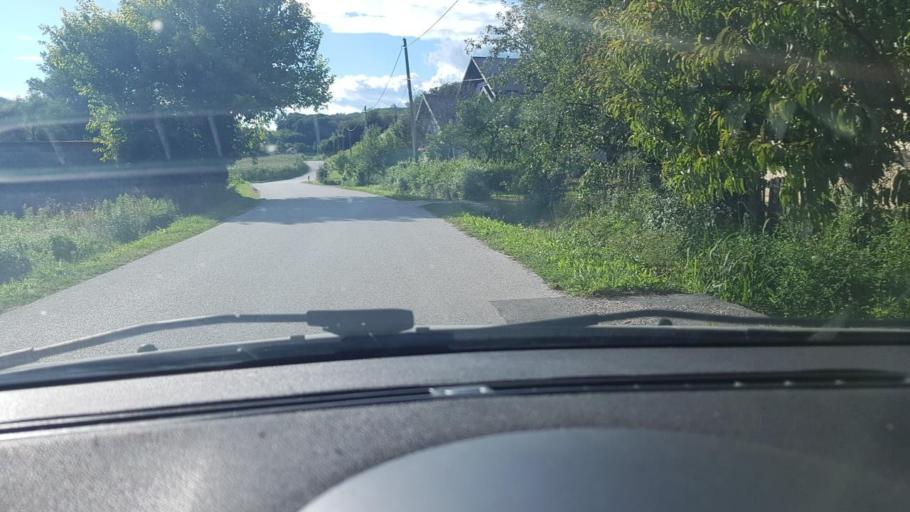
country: HR
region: Krapinsko-Zagorska
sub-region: Grad Krapina
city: Krapina
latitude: 46.1535
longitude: 15.8453
